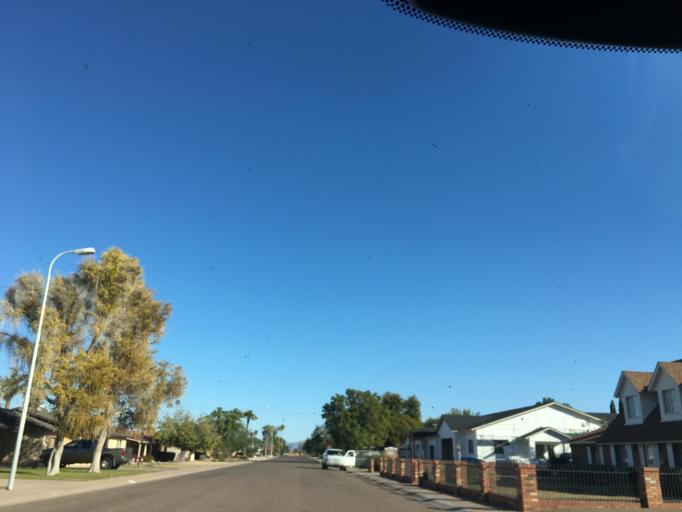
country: US
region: Arizona
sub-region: Maricopa County
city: Scottsdale
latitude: 33.5057
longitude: -111.8974
